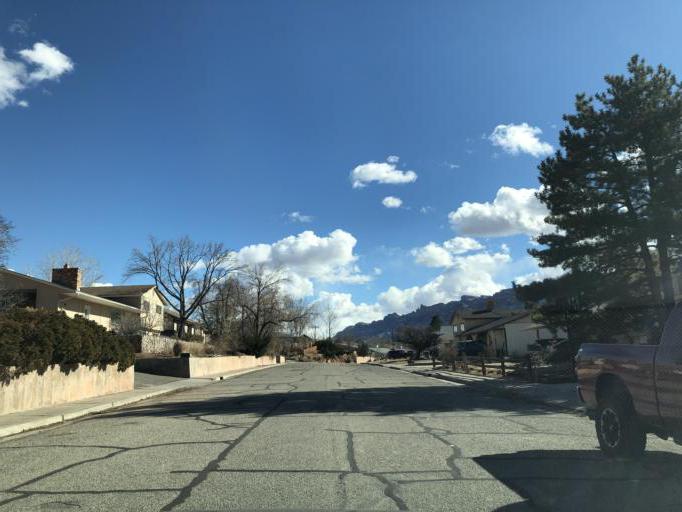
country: US
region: Utah
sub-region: Grand County
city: Moab
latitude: 38.5699
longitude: -109.5352
